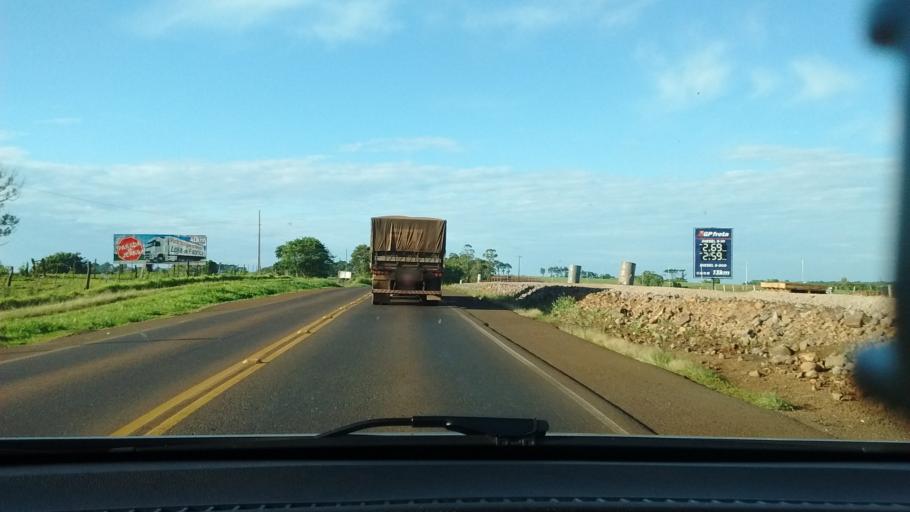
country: BR
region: Parana
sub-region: Cascavel
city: Cascavel
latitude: -25.1676
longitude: -53.6000
